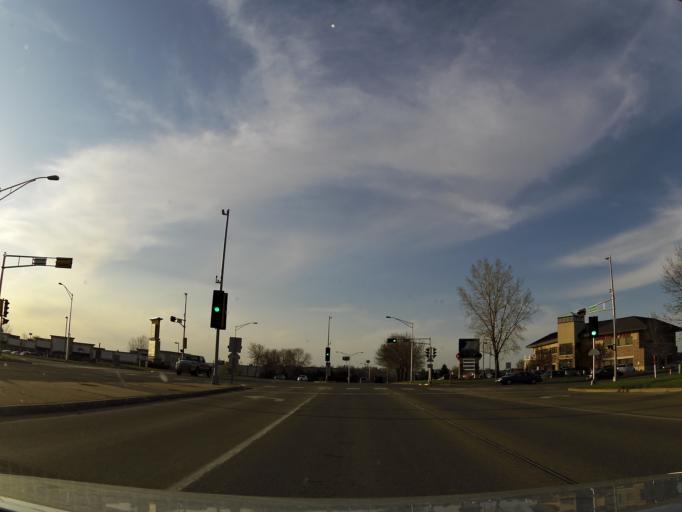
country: US
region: Wisconsin
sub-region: Saint Croix County
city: Hudson
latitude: 44.9538
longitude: -92.7207
